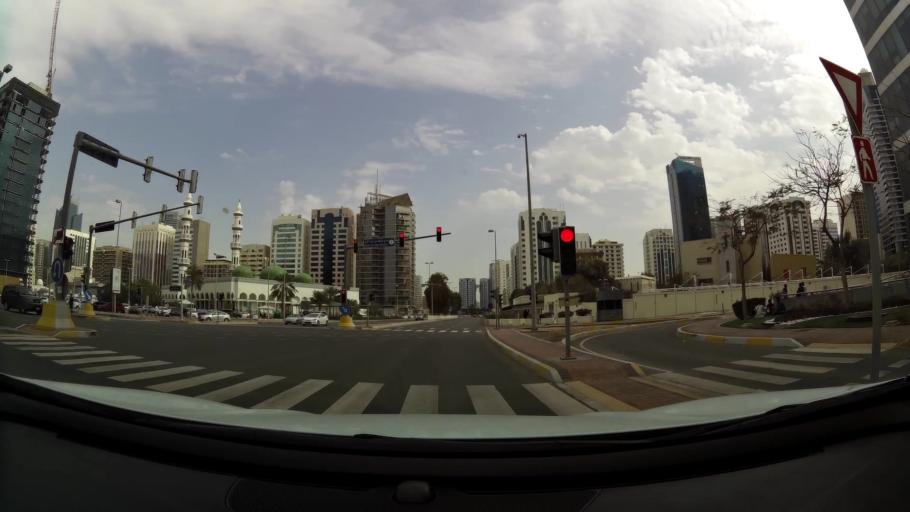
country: AE
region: Abu Dhabi
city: Abu Dhabi
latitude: 24.4852
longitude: 54.3513
